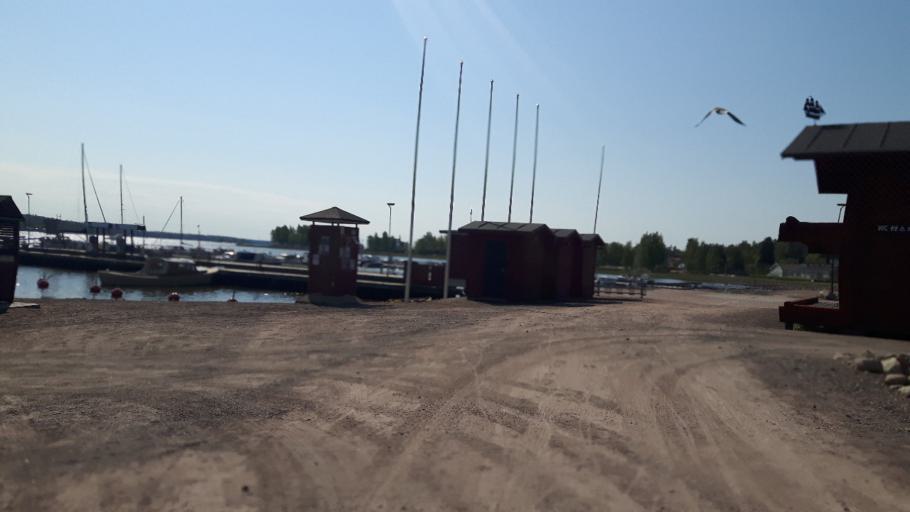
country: FI
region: Uusimaa
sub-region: Loviisa
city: Lovisa
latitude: 60.4525
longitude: 26.2347
